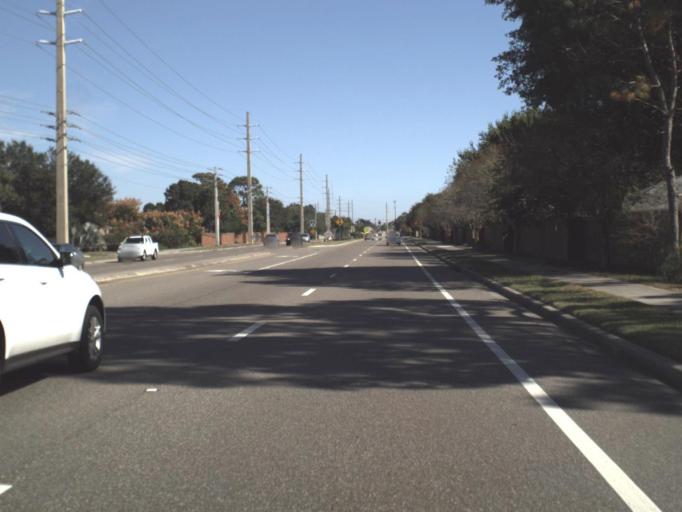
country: US
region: Florida
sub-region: Brevard County
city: South Patrick Shores
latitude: 28.2299
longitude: -80.6877
